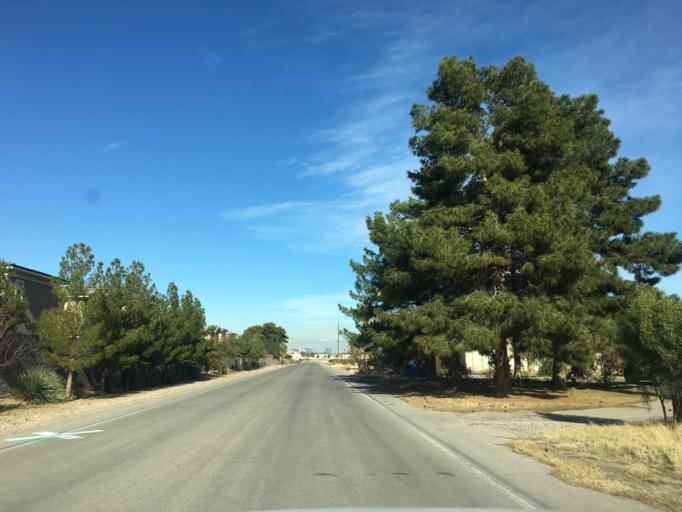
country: US
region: Nevada
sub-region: Clark County
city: Enterprise
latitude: 36.0041
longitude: -115.1681
